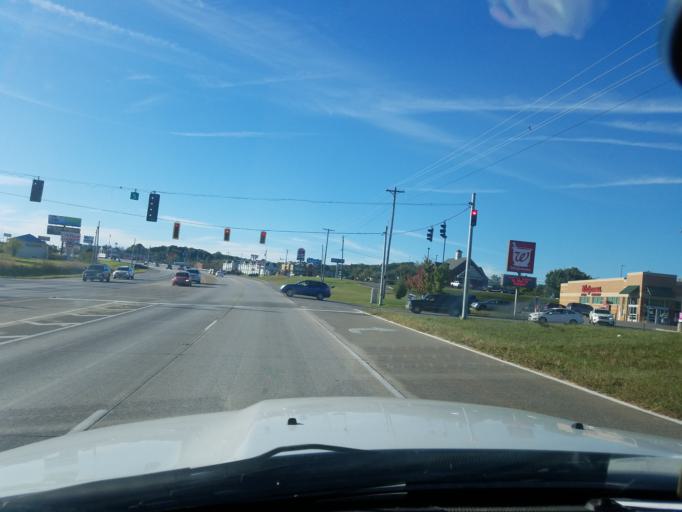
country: US
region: Kentucky
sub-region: Laurel County
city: London
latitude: 37.1104
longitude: -84.0914
